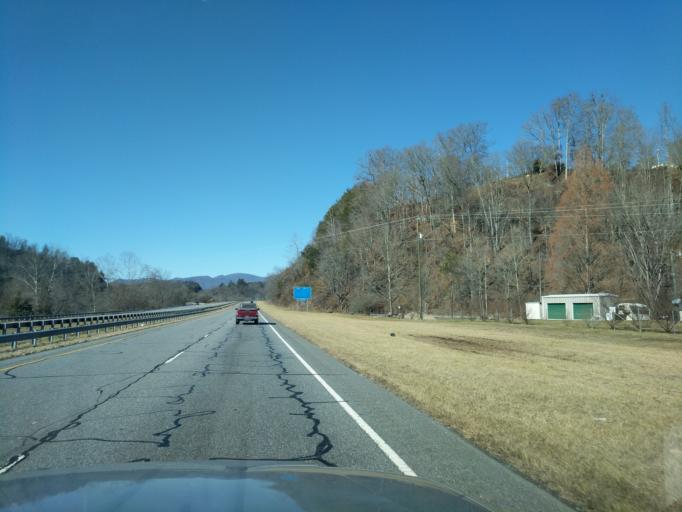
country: US
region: North Carolina
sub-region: Swain County
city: Cherokee
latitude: 35.4259
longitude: -83.3512
